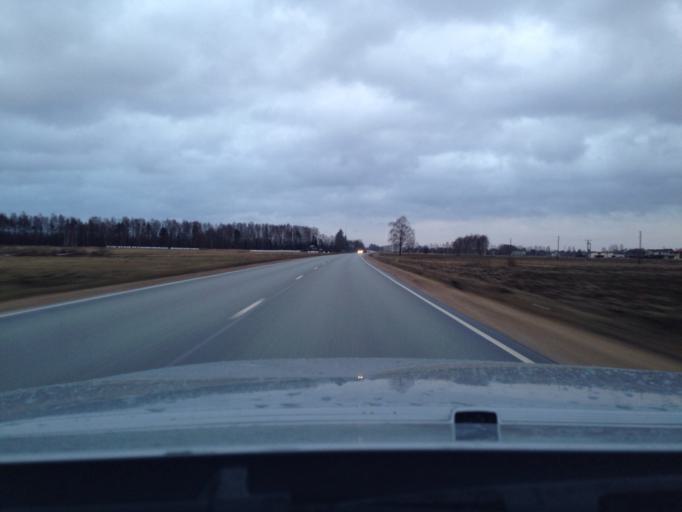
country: LV
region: Marupe
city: Marupe
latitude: 56.8922
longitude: 24.0117
